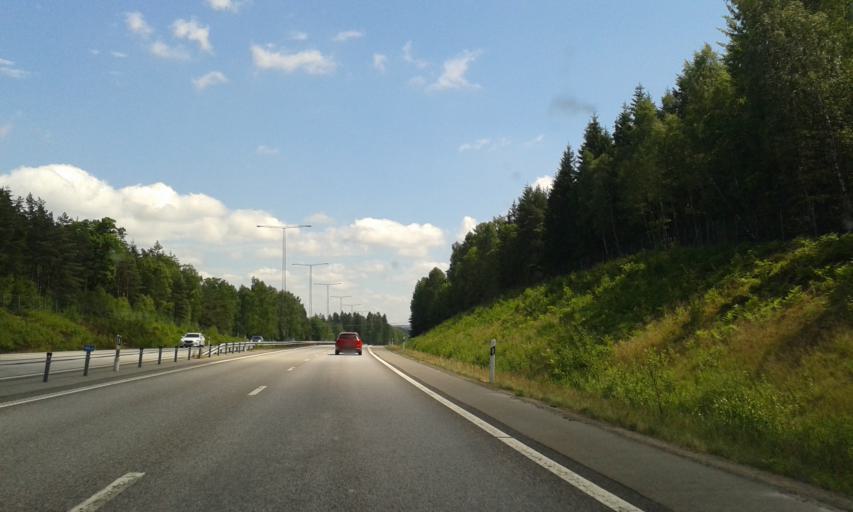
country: SE
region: Kronoberg
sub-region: Vaxjo Kommun
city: Vaexjoe
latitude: 56.8981
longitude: 14.7202
